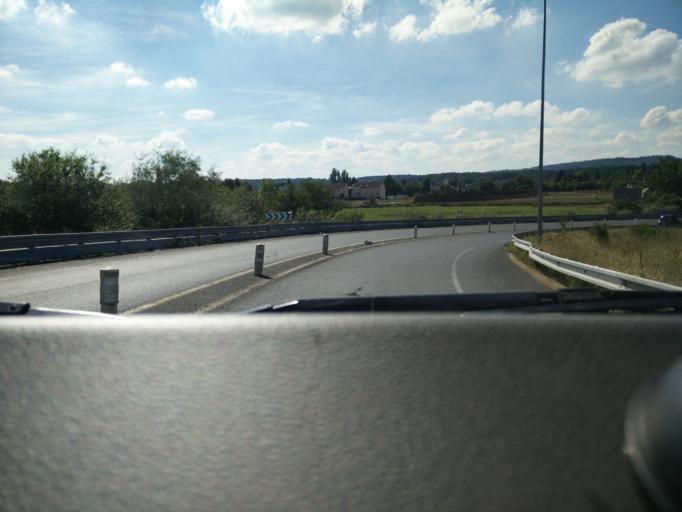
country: FR
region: Lorraine
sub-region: Departement de la Moselle
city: Terville
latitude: 49.3499
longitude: 6.1425
